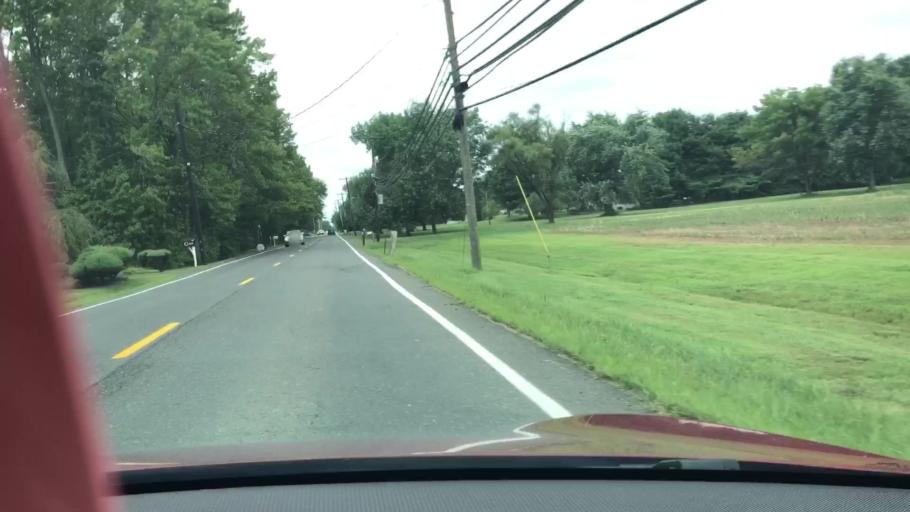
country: US
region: New Jersey
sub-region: Monmouth County
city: Shrewsbury
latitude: 40.1718
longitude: -74.5439
